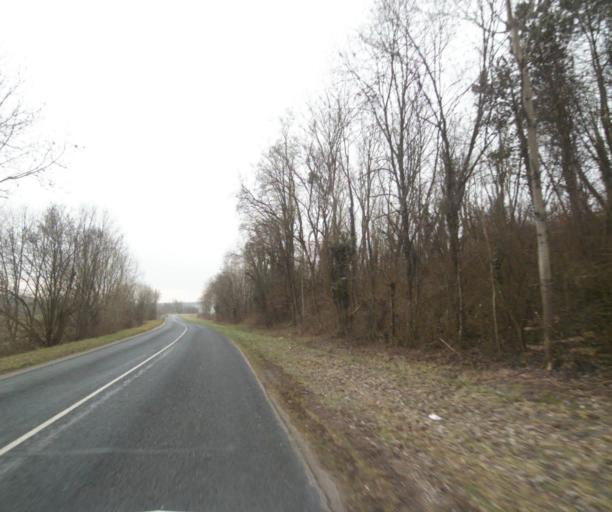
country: FR
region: Champagne-Ardenne
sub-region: Departement de la Haute-Marne
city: Bienville
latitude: 48.5696
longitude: 5.0382
